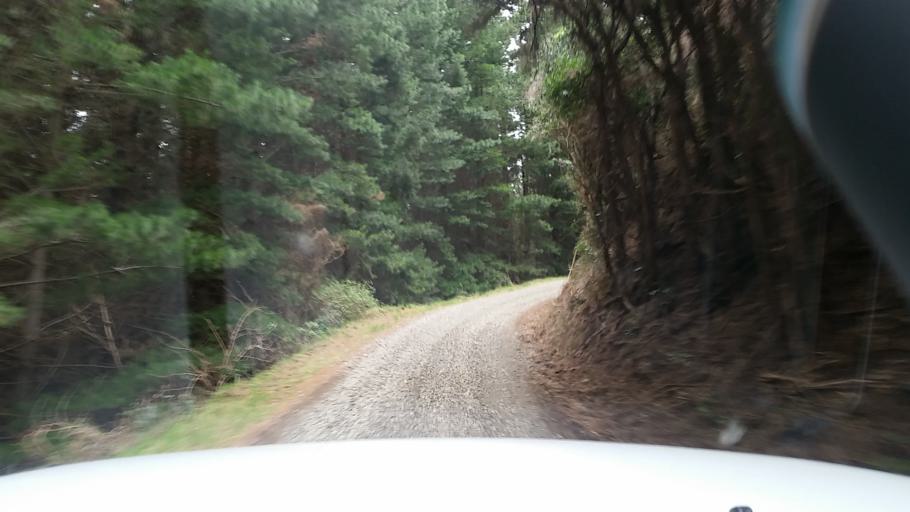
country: NZ
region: Canterbury
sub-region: Christchurch City
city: Christchurch
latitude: -43.6975
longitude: 172.7816
